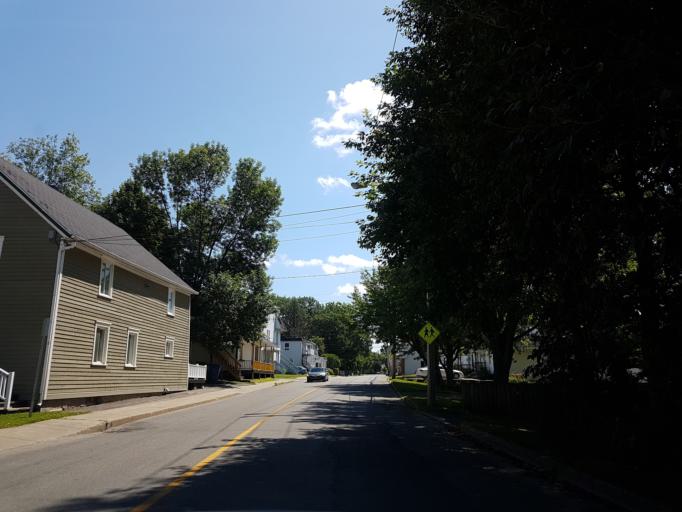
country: CA
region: Quebec
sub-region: Mauricie
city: Nicolet
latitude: 46.2296
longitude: -72.6242
